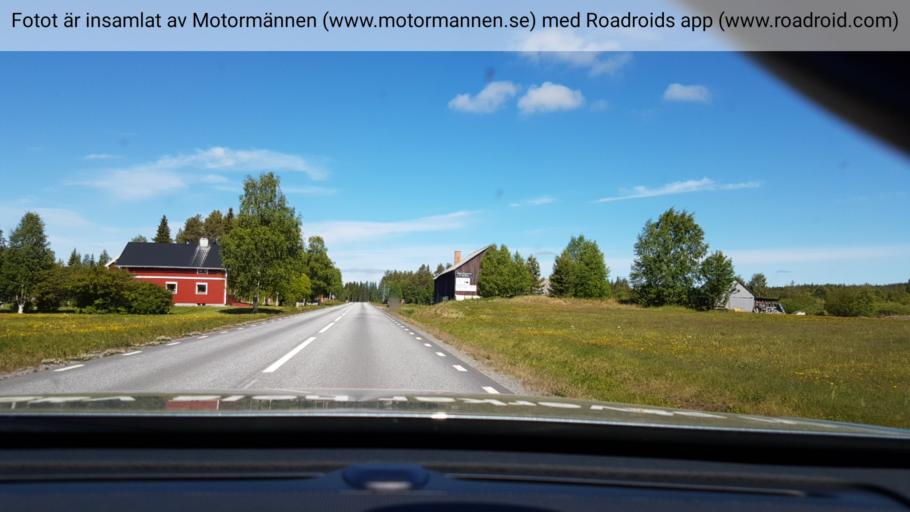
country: SE
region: Vaesterbotten
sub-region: Vilhelmina Kommun
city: Vilhelmina
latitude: 64.4523
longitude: 16.8173
